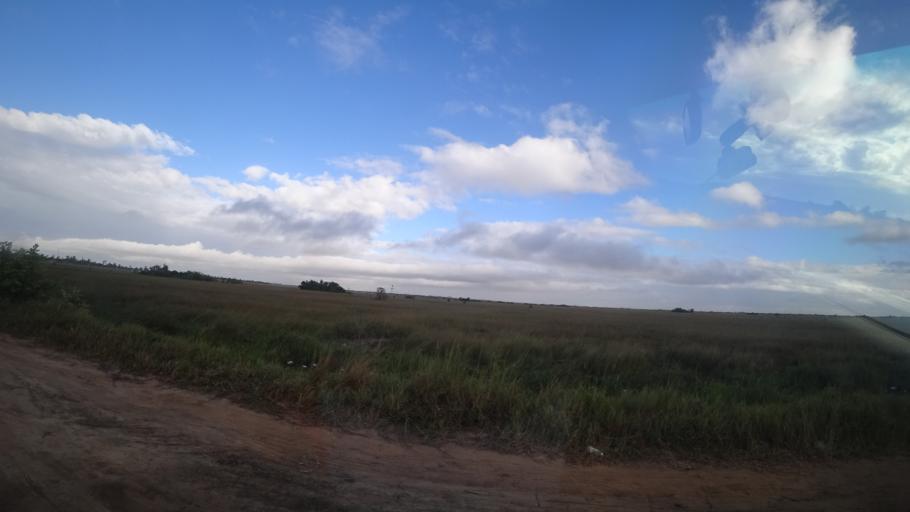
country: MZ
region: Sofala
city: Beira
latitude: -19.7070
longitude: 35.0178
